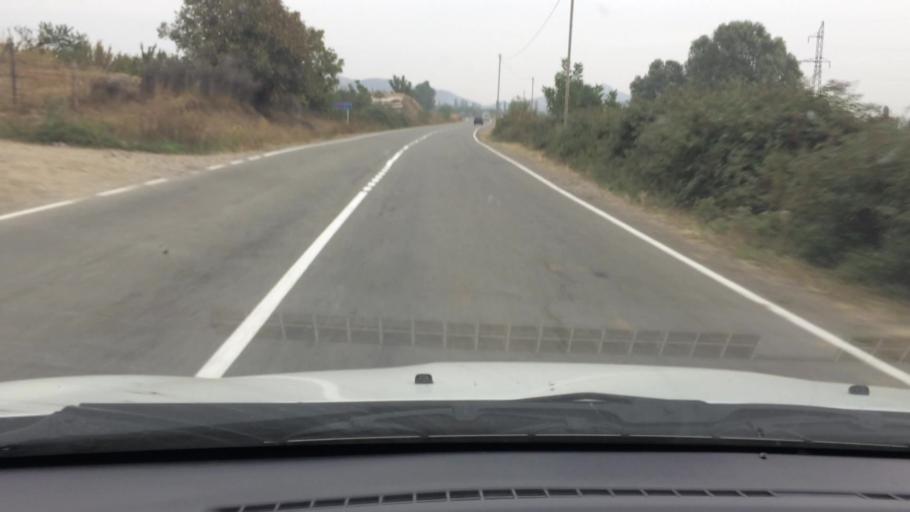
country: GE
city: Naghvarevi
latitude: 41.3111
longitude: 44.7923
